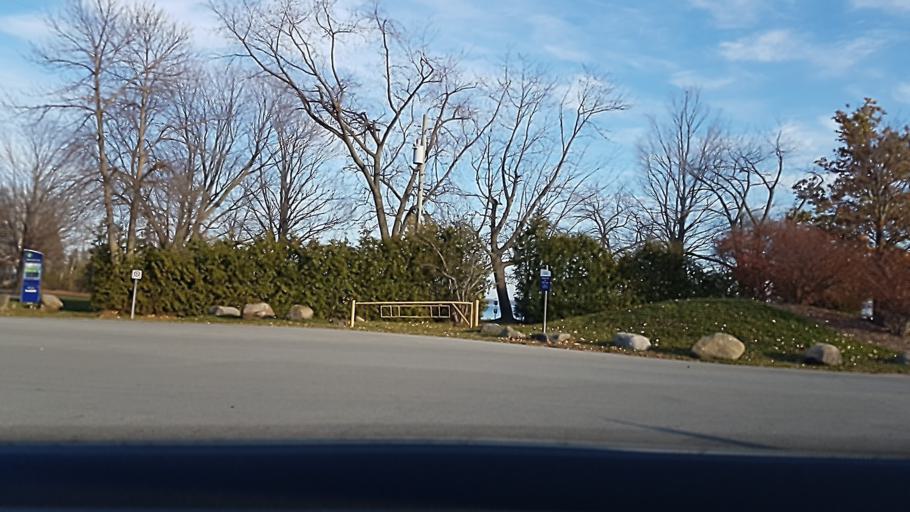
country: CA
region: Ontario
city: Keswick
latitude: 44.3189
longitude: -79.5337
